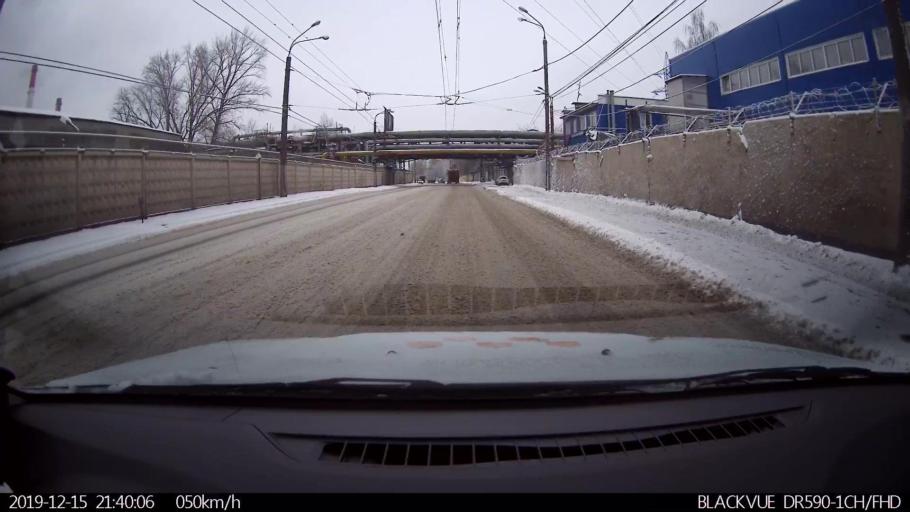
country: RU
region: Nizjnij Novgorod
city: Nizhniy Novgorod
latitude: 56.2400
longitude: 43.8941
